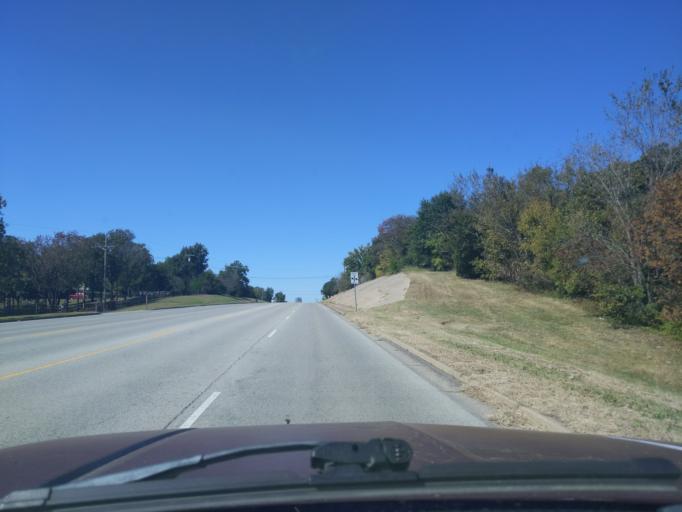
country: US
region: Oklahoma
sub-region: Creek County
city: Kiefer
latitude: 35.9885
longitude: -96.0659
